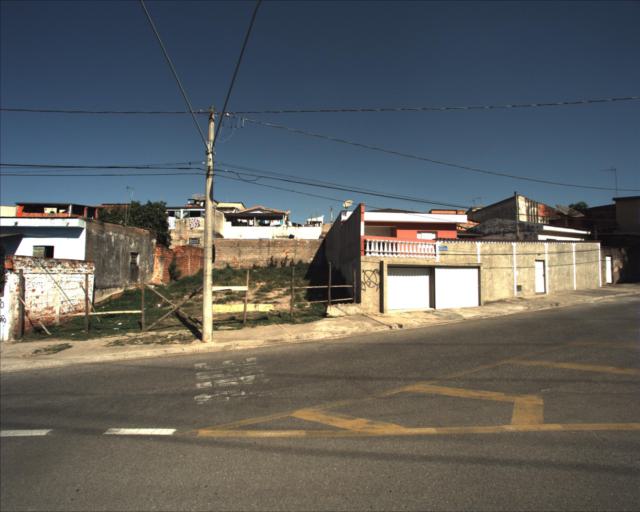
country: BR
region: Sao Paulo
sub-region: Sorocaba
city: Sorocaba
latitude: -23.4550
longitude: -47.4749
